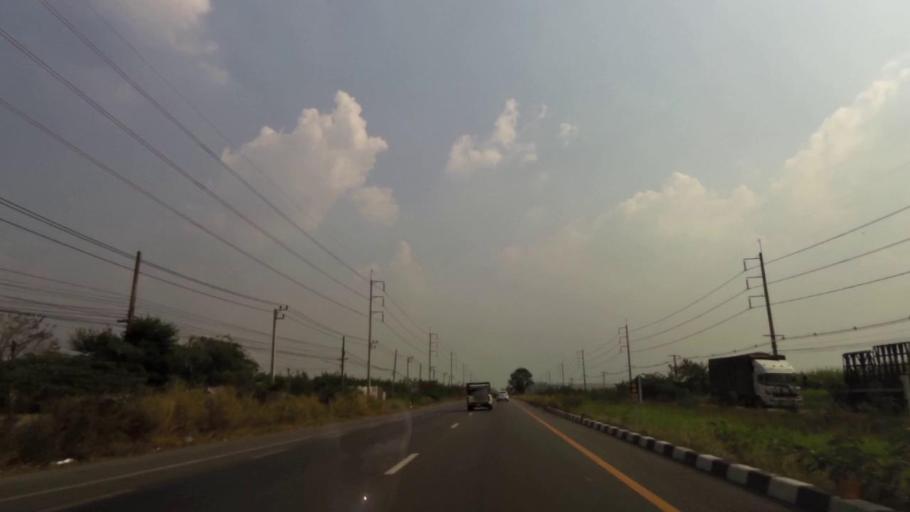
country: TH
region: Chon Buri
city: Nong Yai
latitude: 13.1889
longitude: 101.2526
